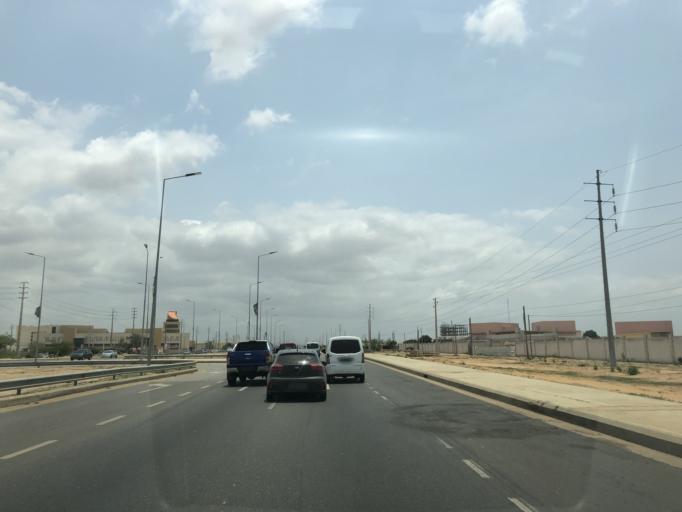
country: AO
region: Luanda
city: Luanda
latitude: -8.9574
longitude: 13.2575
